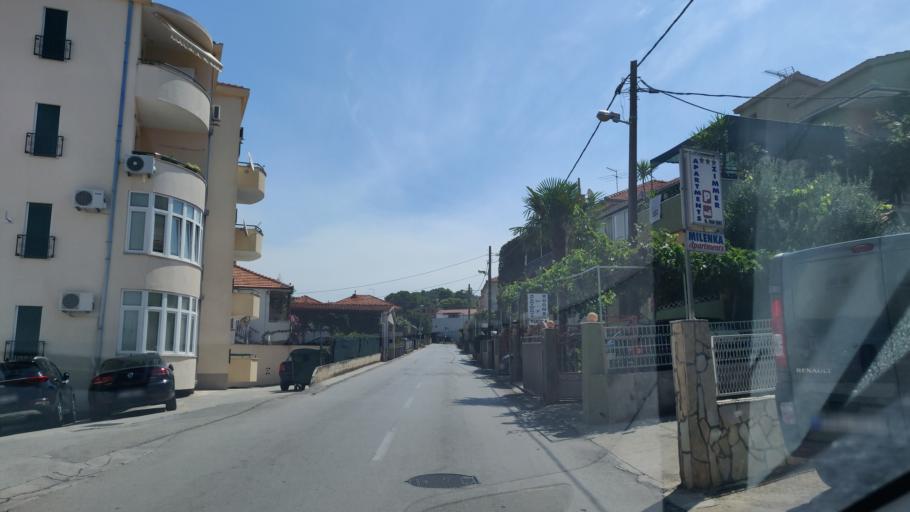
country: HR
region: Splitsko-Dalmatinska
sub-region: Grad Trogir
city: Trogir
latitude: 43.5122
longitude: 16.2490
